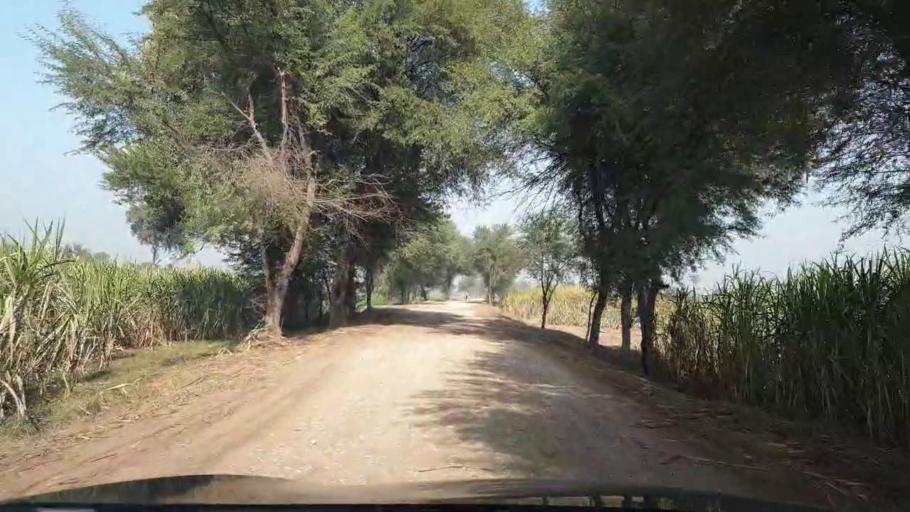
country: PK
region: Sindh
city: Ubauro
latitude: 28.1168
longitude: 69.7511
